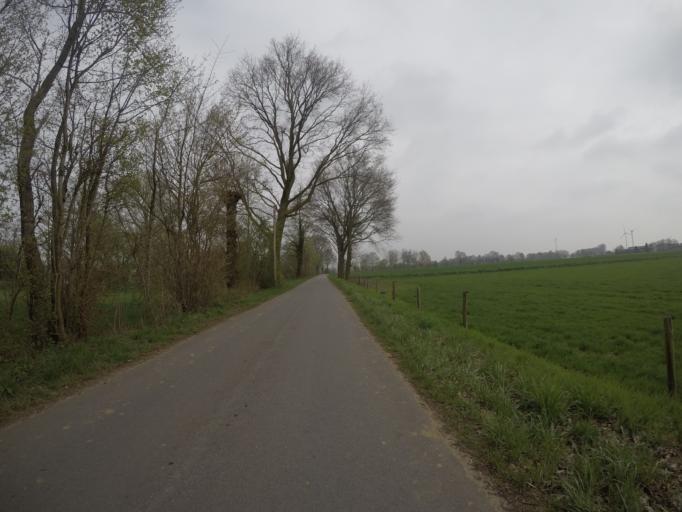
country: NL
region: Gelderland
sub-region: Gemeente Aalten
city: Aalten
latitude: 51.8787
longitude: 6.5521
